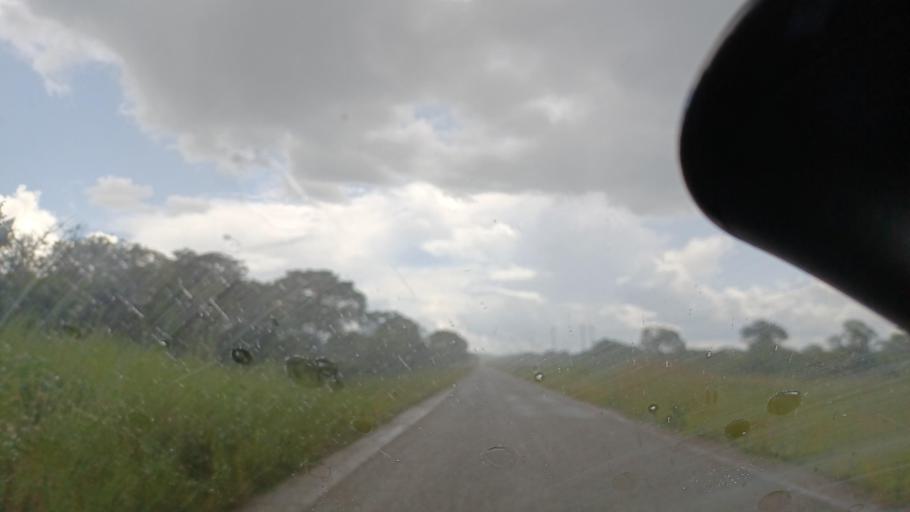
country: ZM
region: North-Western
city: Kasempa
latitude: -13.0990
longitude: 25.9010
